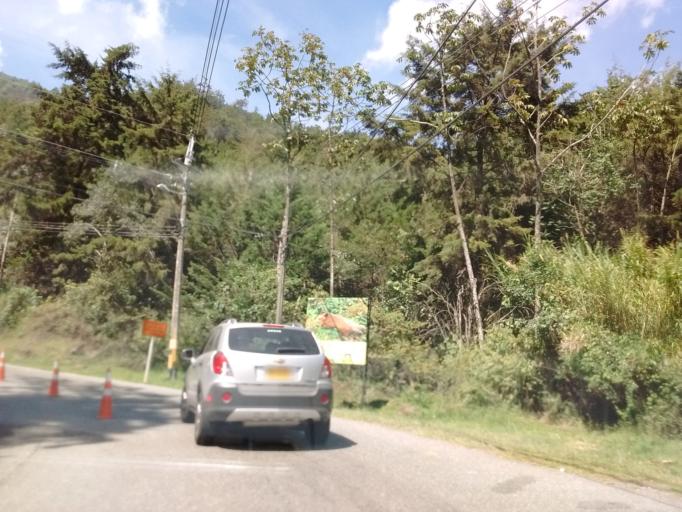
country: CO
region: Antioquia
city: Medellin
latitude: 6.2266
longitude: -75.5166
